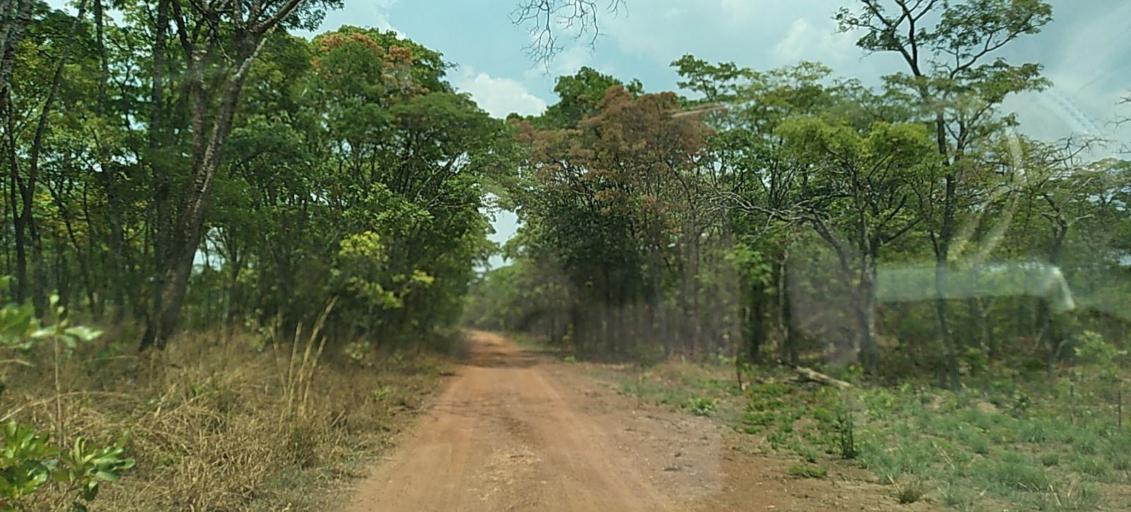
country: ZM
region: Copperbelt
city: Chingola
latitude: -12.7821
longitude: 27.6682
